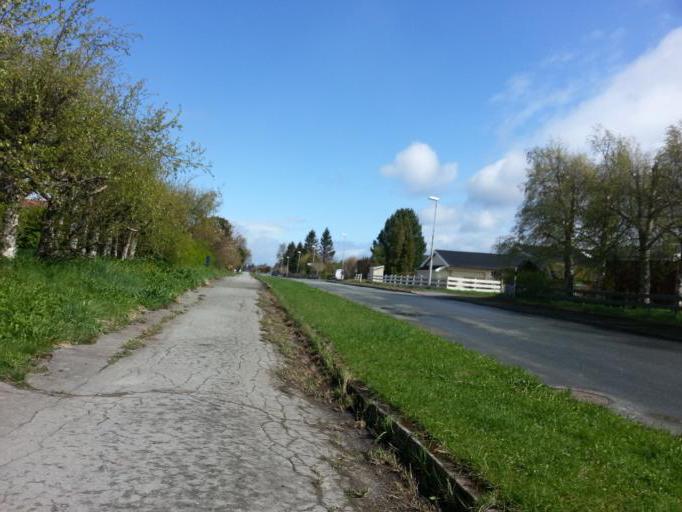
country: NO
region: Sor-Trondelag
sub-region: Trondheim
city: Trondheim
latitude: 63.3902
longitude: 10.3628
